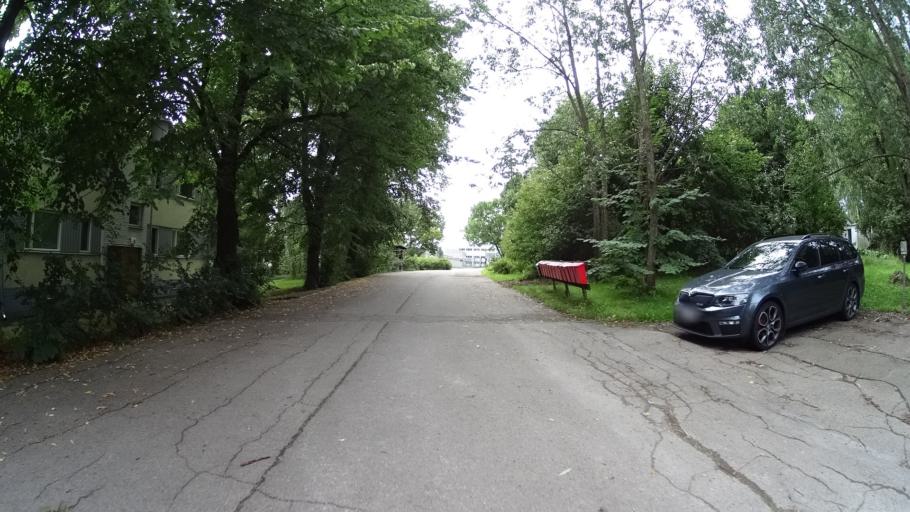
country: FI
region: Uusimaa
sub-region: Helsinki
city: Teekkarikylae
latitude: 60.2664
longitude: 24.8969
